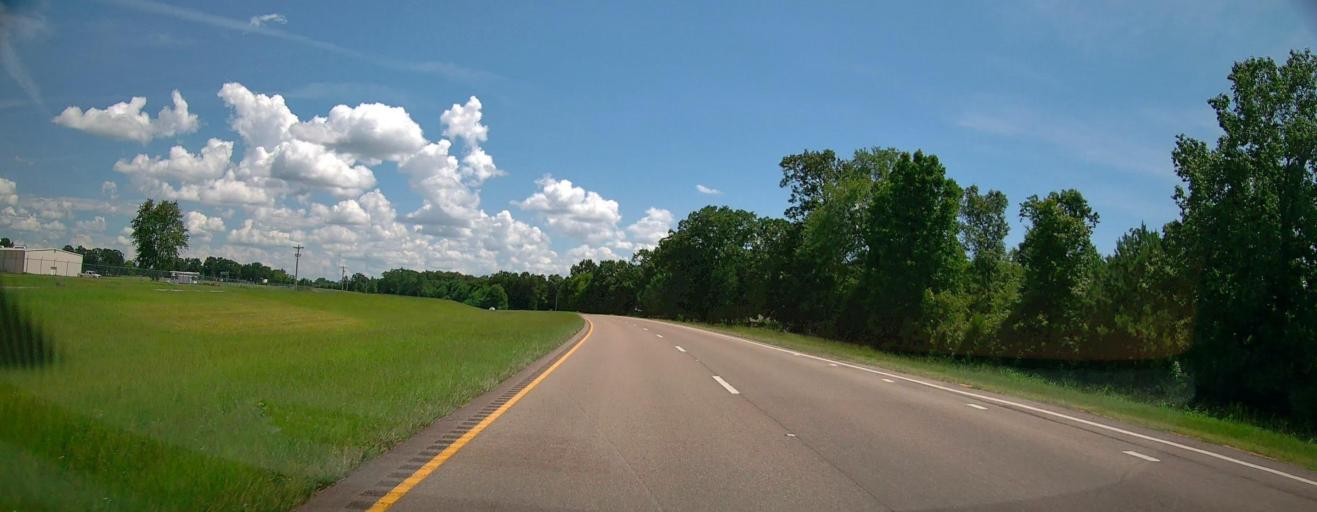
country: US
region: Mississippi
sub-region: Lee County
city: Nettleton
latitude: 33.9647
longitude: -88.6139
